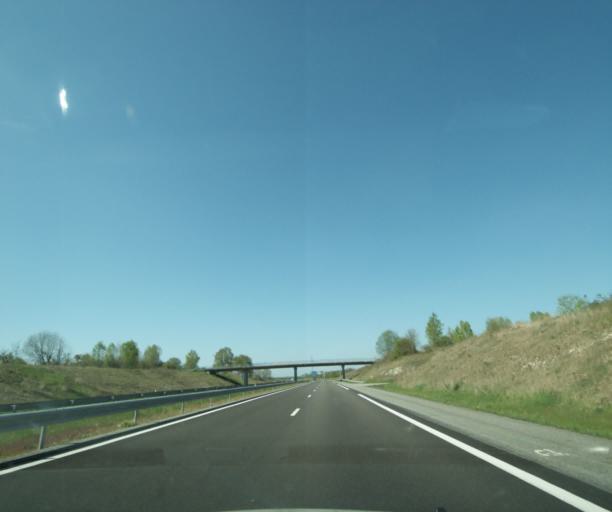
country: FR
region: Bourgogne
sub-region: Departement de la Nievre
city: Neuvy-sur-Loire
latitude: 47.5643
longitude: 2.8806
